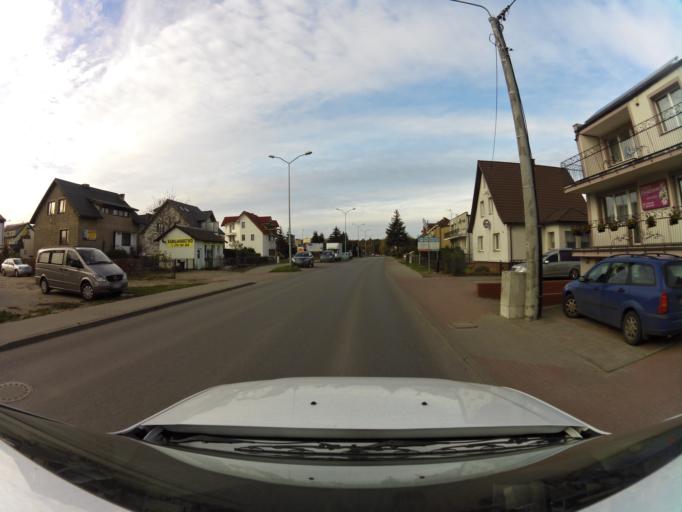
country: PL
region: West Pomeranian Voivodeship
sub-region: Powiat gryficki
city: Gryfice
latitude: 53.9209
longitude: 15.1861
